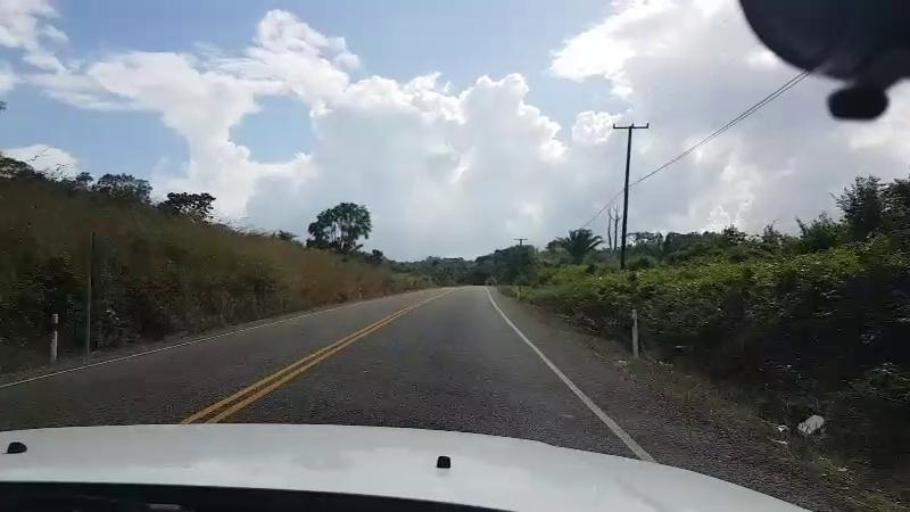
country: BZ
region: Cayo
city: Belmopan
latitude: 17.2296
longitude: -88.7793
